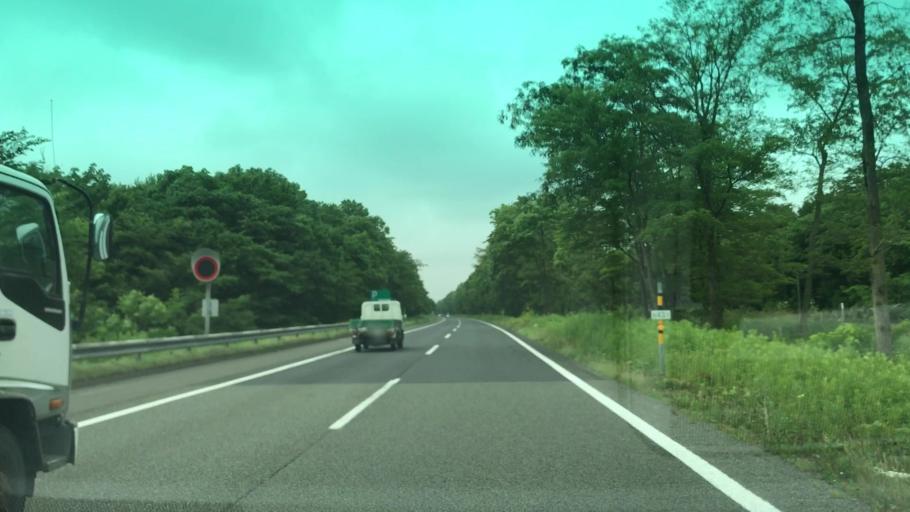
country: JP
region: Hokkaido
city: Chitose
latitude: 42.7461
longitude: 141.6486
